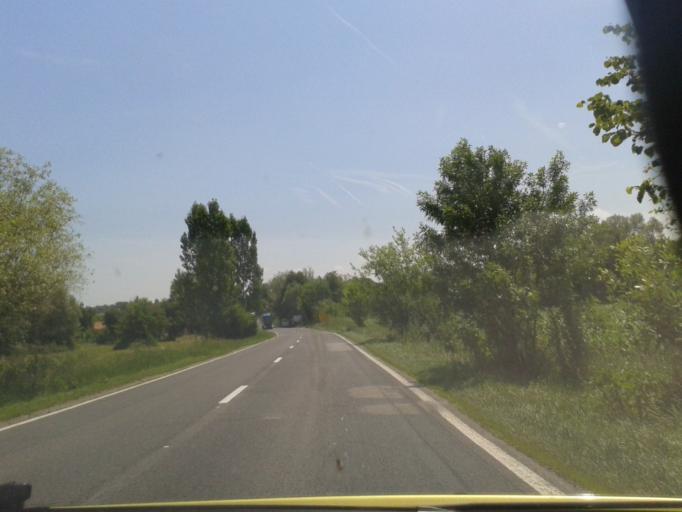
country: RO
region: Timis
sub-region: Comuna Curtea
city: Curtea
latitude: 45.8488
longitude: 22.3045
